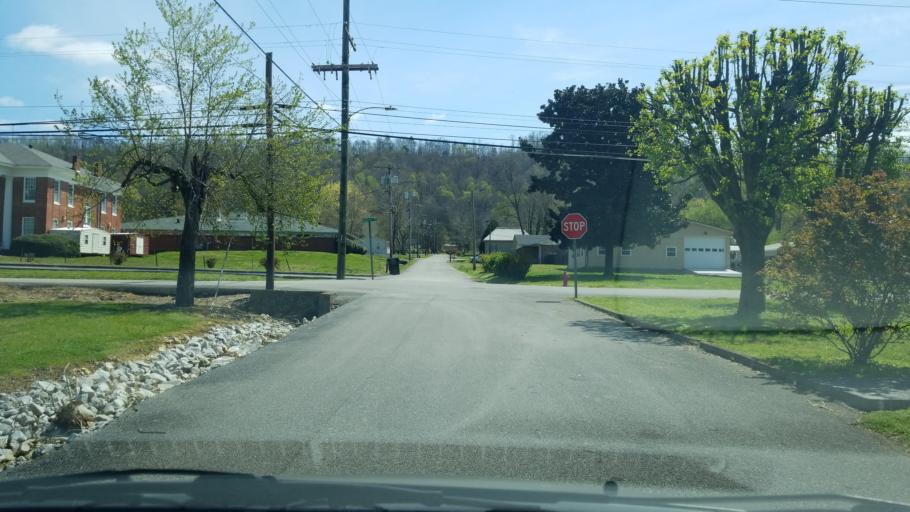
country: US
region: Tennessee
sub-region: Hamilton County
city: Collegedale
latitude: 35.0713
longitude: -85.0612
